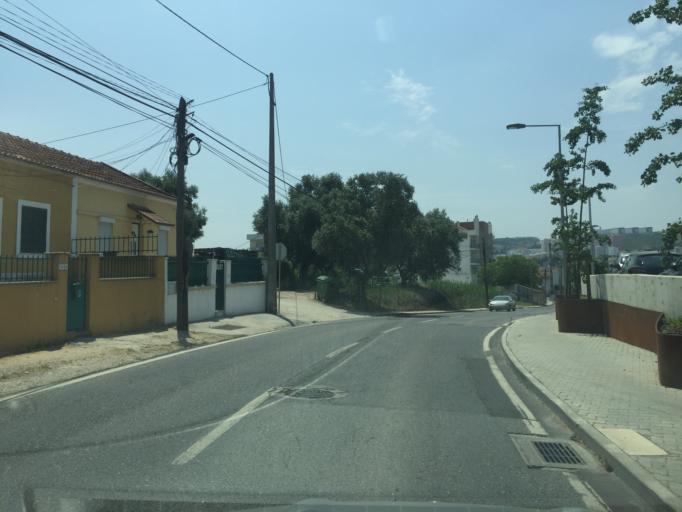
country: PT
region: Lisbon
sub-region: Loures
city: Loures
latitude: 38.8412
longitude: -9.1769
